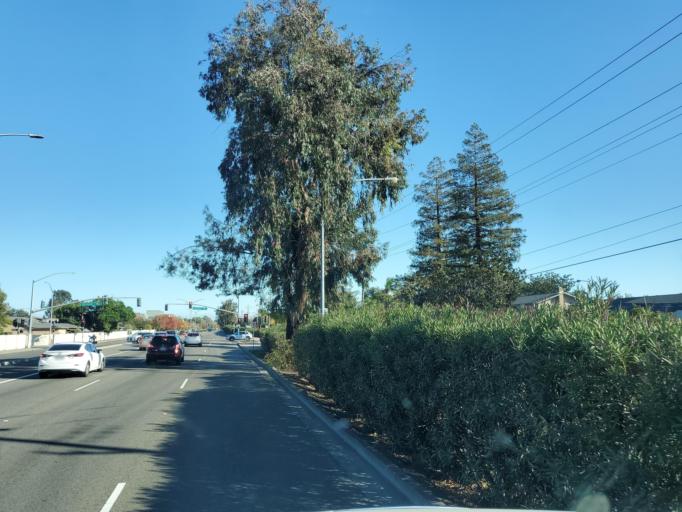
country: US
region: California
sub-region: San Joaquin County
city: Lincoln Village
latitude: 38.0212
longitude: -121.3526
